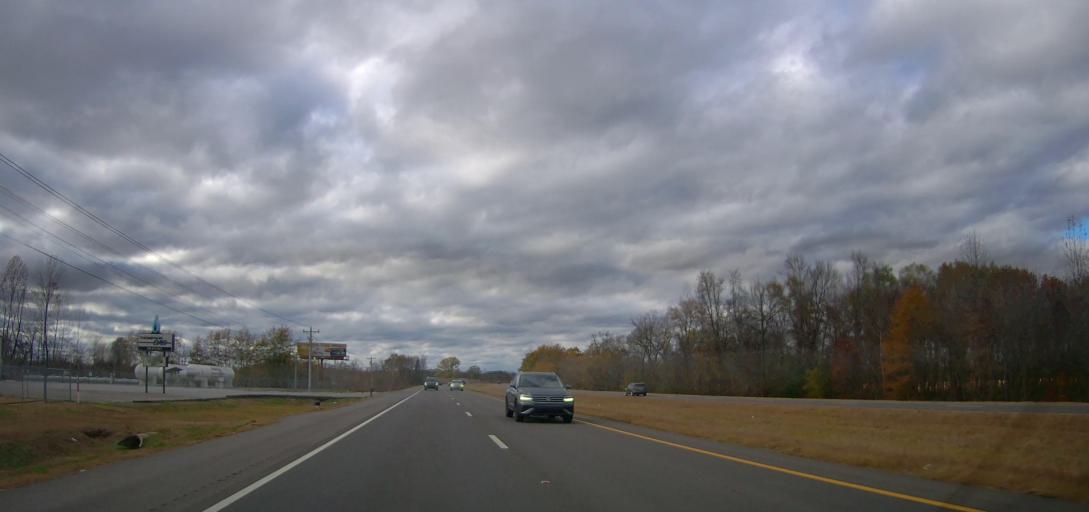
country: US
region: Alabama
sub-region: Lawrence County
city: Moulton
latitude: 34.4655
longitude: -87.2578
